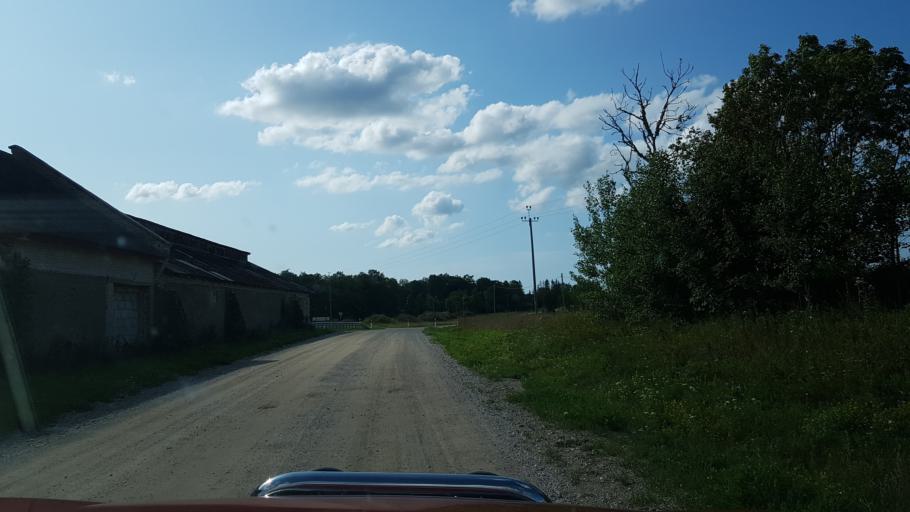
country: EE
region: Harju
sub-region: Paldiski linn
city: Paldiski
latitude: 59.1996
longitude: 23.9436
